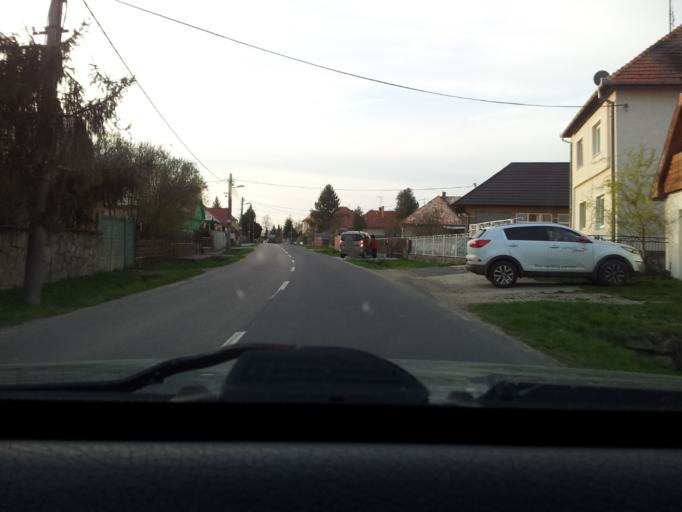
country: SK
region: Nitriansky
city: Levice
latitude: 48.2649
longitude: 18.5987
